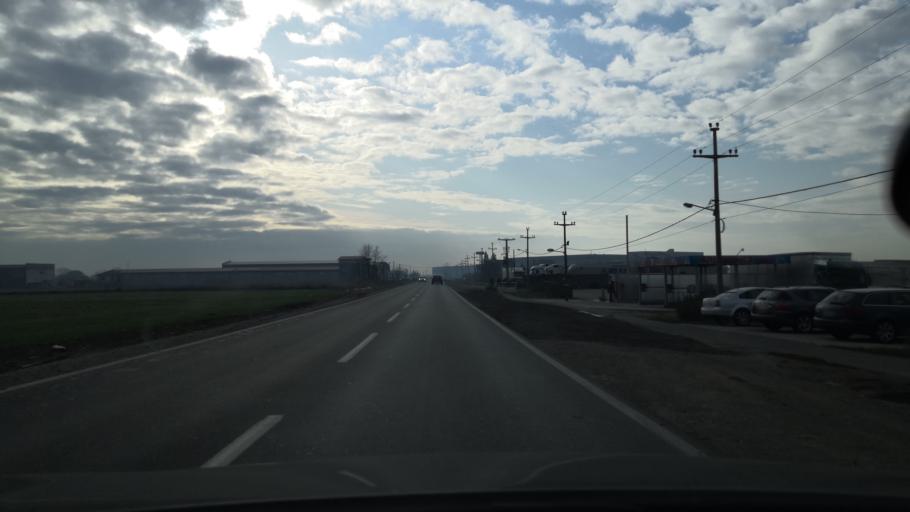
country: RS
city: Ugrinovci
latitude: 44.8591
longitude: 20.2050
